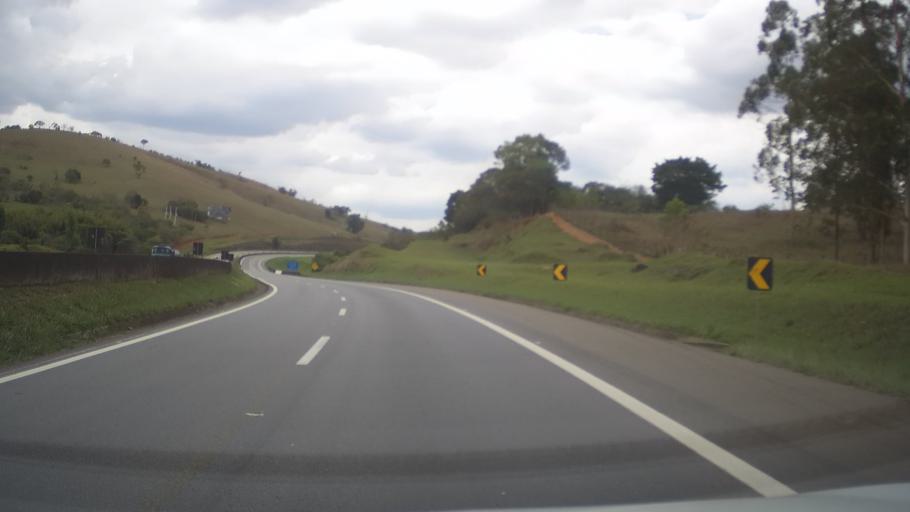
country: BR
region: Minas Gerais
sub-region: Tres Coracoes
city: Tres Coracoes
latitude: -21.5223
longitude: -45.2238
